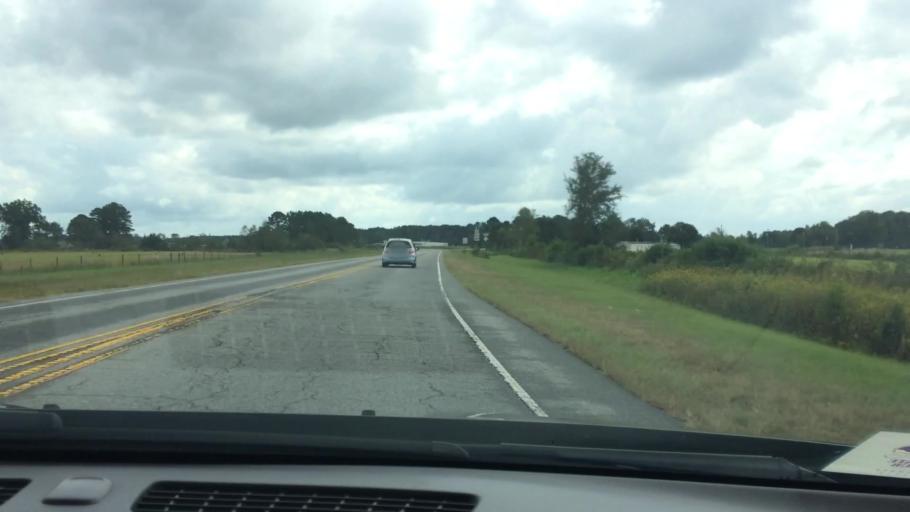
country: US
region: North Carolina
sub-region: Pitt County
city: Farmville
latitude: 35.6119
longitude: -77.6584
